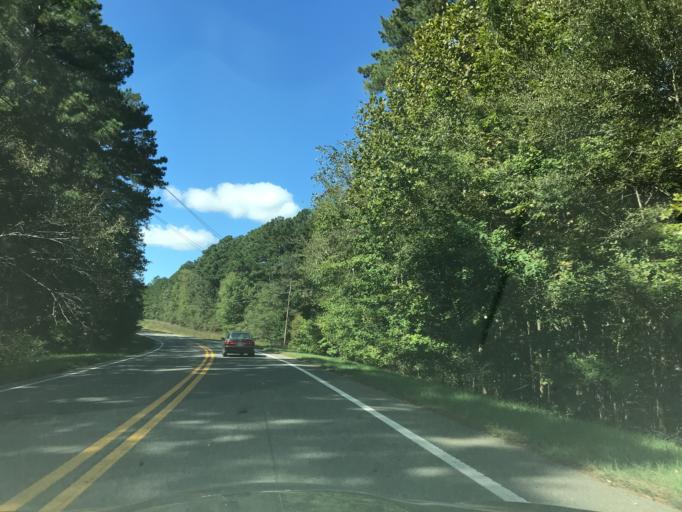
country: US
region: North Carolina
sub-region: Durham County
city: Gorman
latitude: 35.9817
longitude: -78.7422
